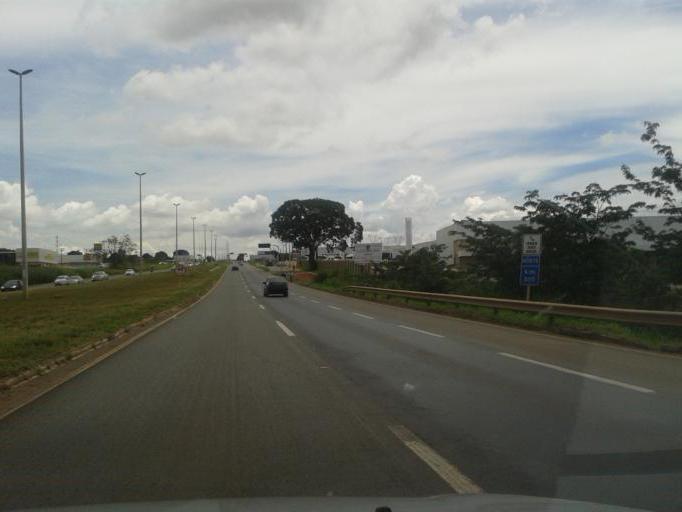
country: BR
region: Goias
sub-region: Aparecida De Goiania
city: Aparecida de Goiania
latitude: -16.8320
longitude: -49.2432
